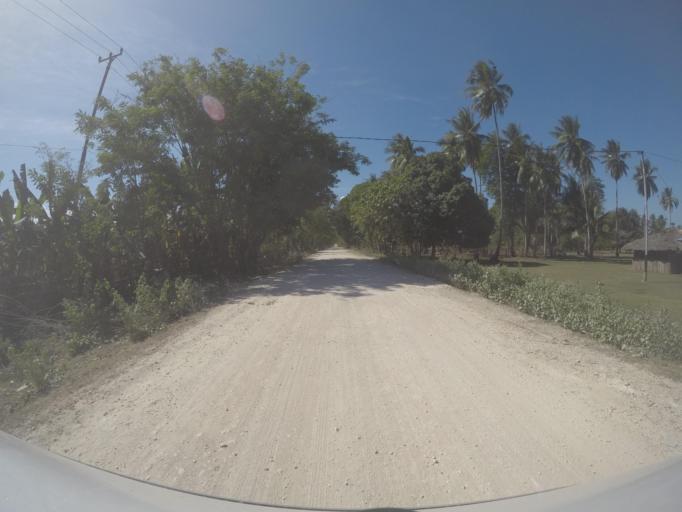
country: TL
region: Viqueque
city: Viqueque
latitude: -8.8834
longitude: 126.5072
